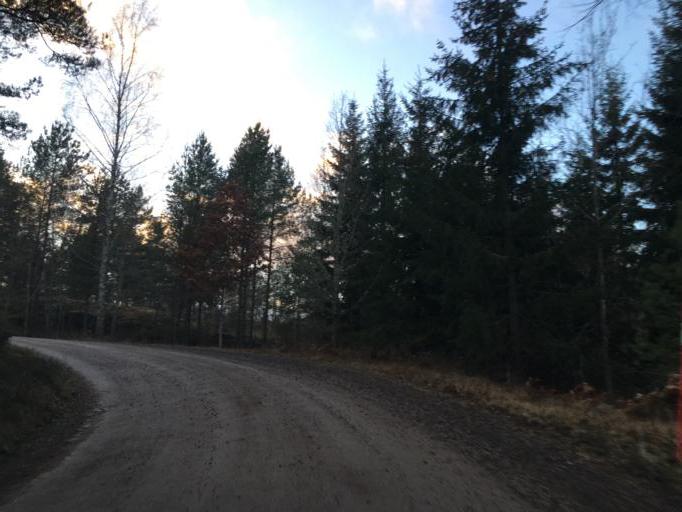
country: SE
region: Kalmar
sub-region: Vasterviks Kommun
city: Vaestervik
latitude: 57.6004
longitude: 16.5230
